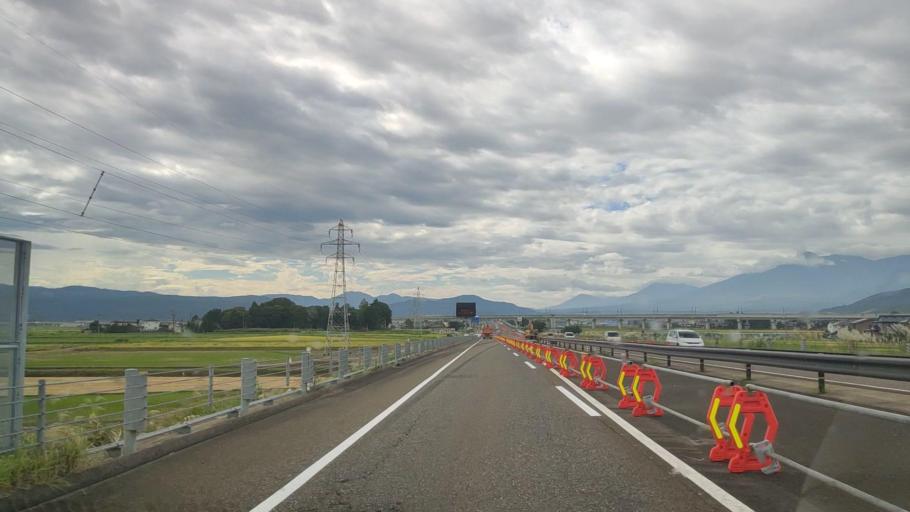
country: JP
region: Niigata
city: Joetsu
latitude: 37.0761
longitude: 138.2655
